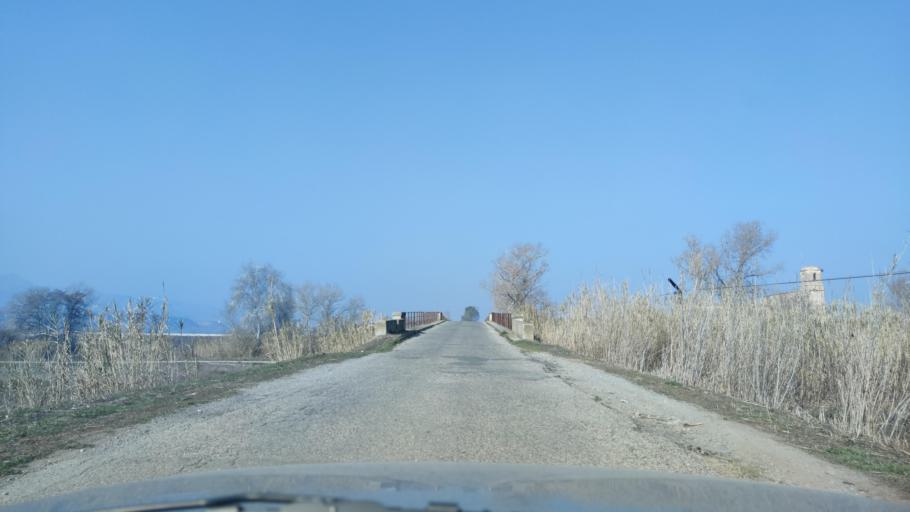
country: ES
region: Catalonia
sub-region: Provincia de Lleida
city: la Granja d'Escarp
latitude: 41.4288
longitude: 0.3550
